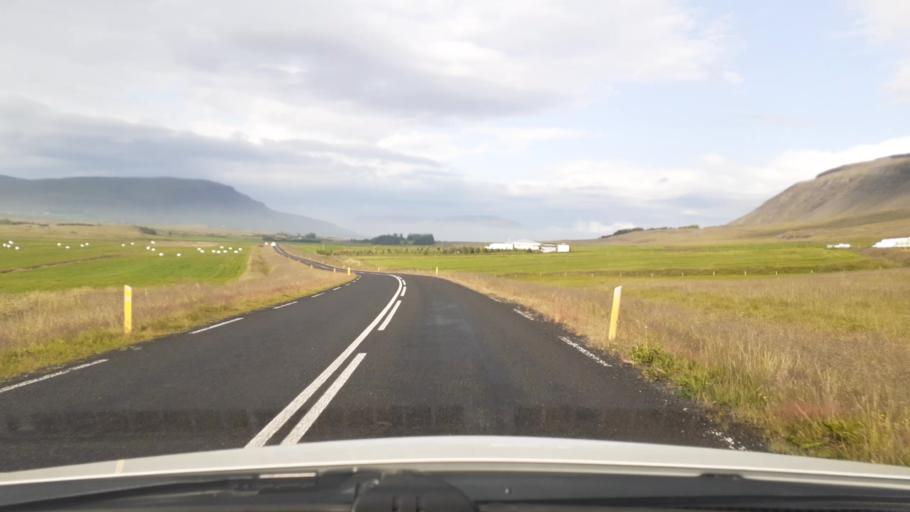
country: IS
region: Capital Region
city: Mosfellsbaer
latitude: 64.3427
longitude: -21.5650
